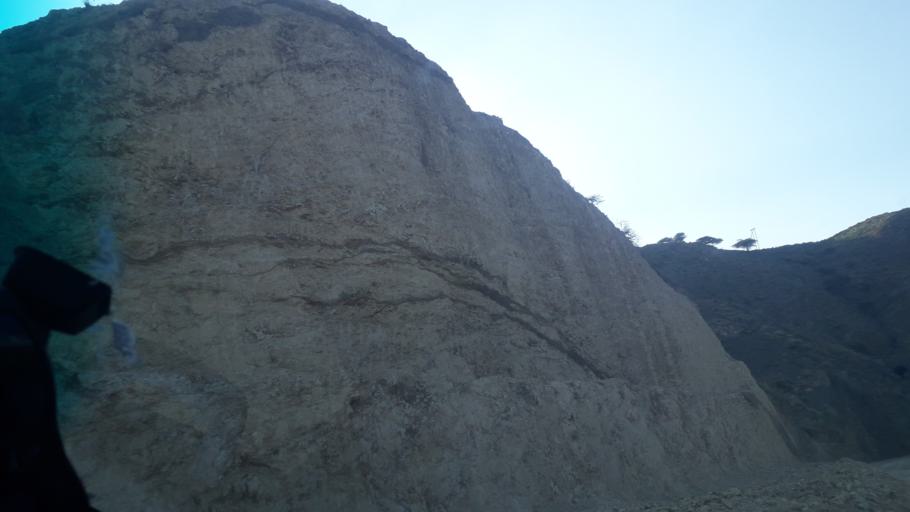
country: ET
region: Amhara
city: Dese
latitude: 11.5199
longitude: 39.2515
